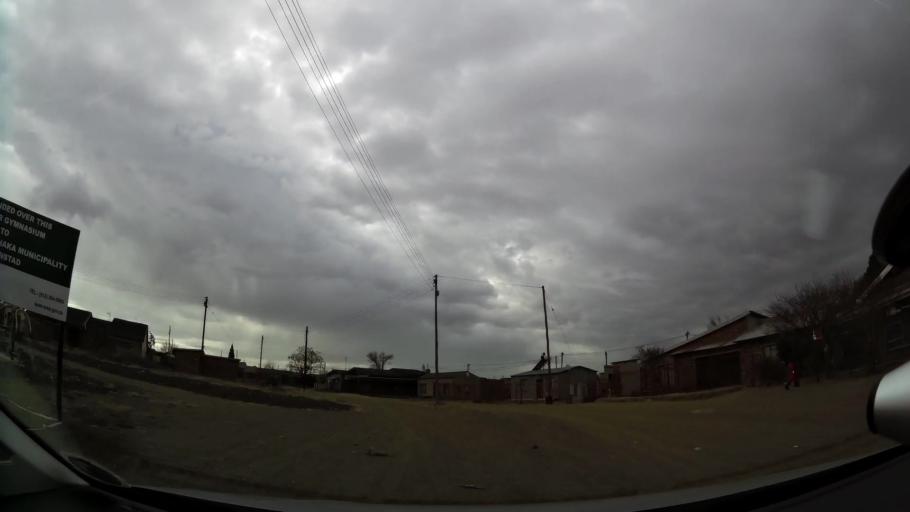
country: ZA
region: Orange Free State
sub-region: Fezile Dabi District Municipality
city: Kroonstad
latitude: -27.6496
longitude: 27.2072
